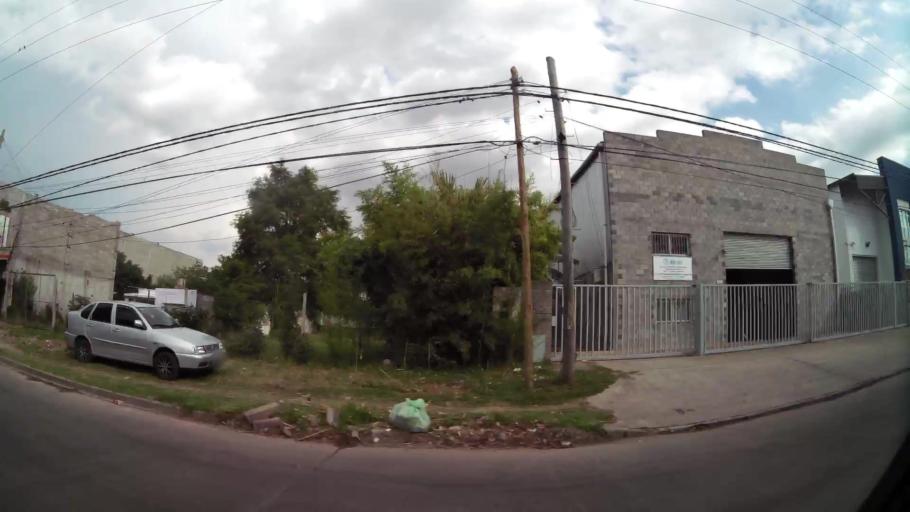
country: AR
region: Buenos Aires
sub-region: Partido de Tigre
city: Tigre
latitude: -34.4772
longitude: -58.6268
